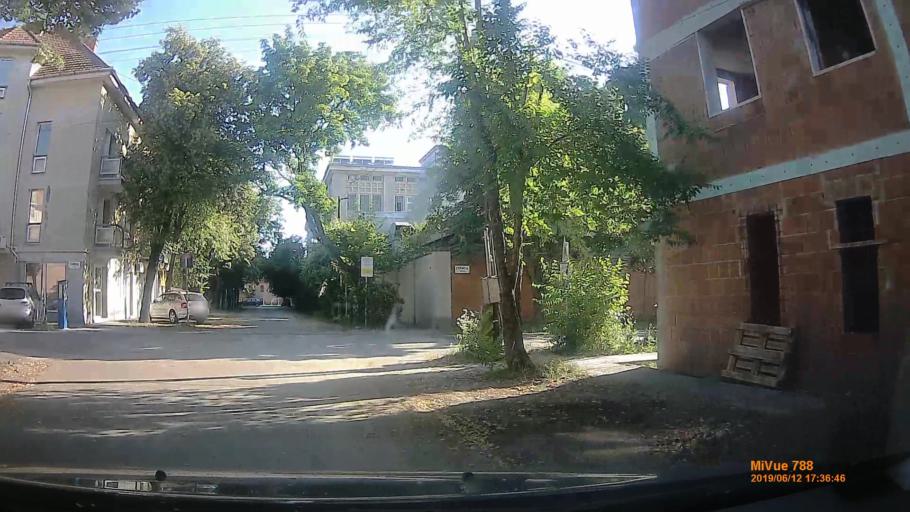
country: HU
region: Csongrad
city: Szeged
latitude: 46.2574
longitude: 20.1360
